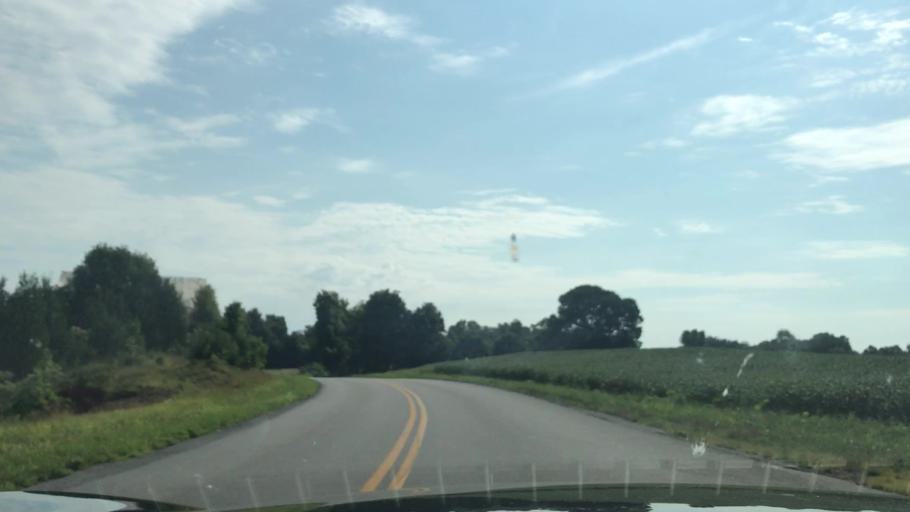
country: US
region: Kentucky
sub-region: Green County
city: Greensburg
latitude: 37.2246
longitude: -85.6627
